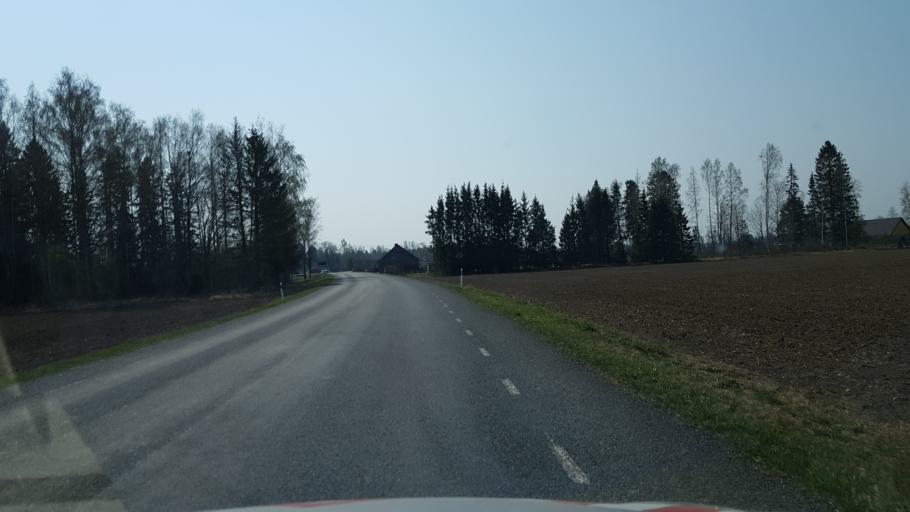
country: EE
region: Raplamaa
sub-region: Kehtna vald
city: Kehtna
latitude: 59.0137
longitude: 24.9203
